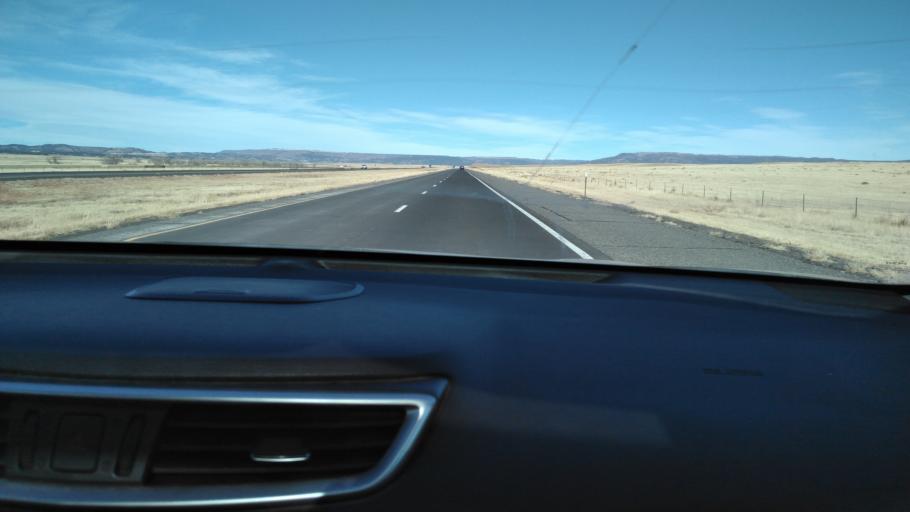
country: US
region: New Mexico
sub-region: Colfax County
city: Raton
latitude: 36.7378
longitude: -104.4556
